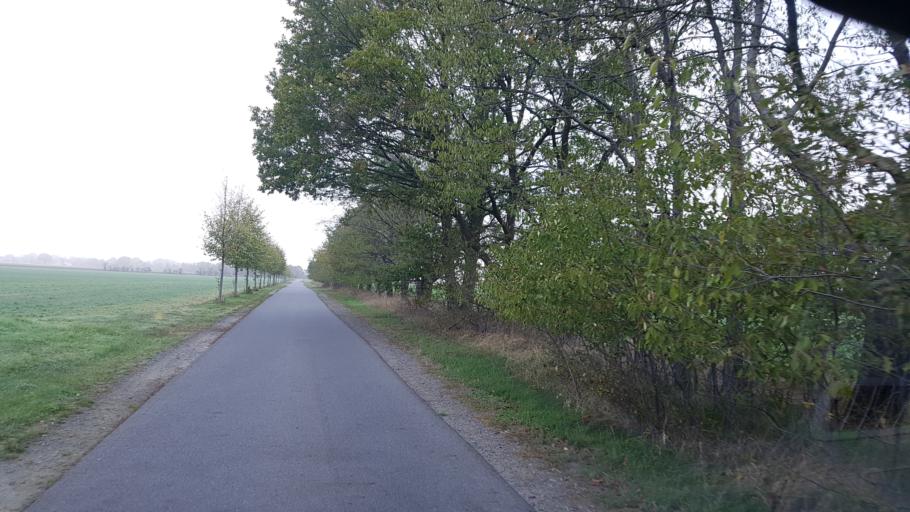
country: DE
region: Brandenburg
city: Schonewalde
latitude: 51.6760
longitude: 13.6248
